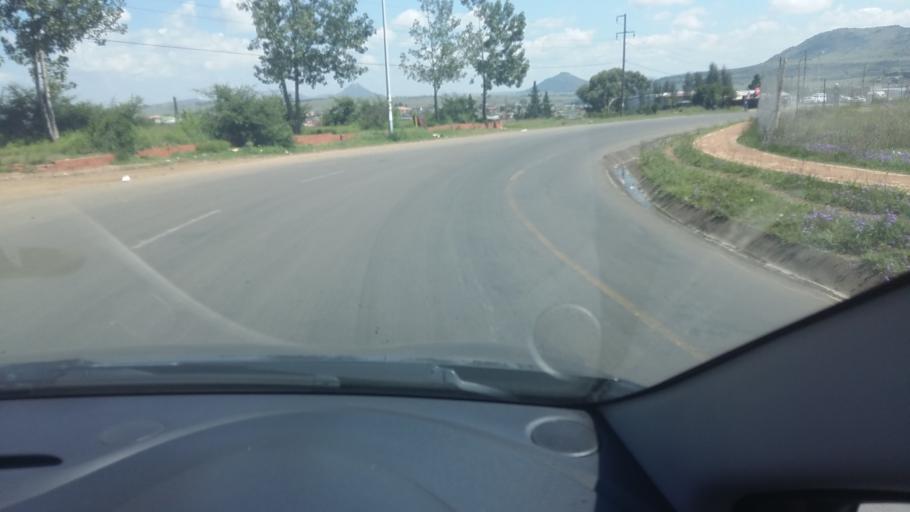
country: LS
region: Maseru
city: Maseru
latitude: -29.3392
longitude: 27.4570
